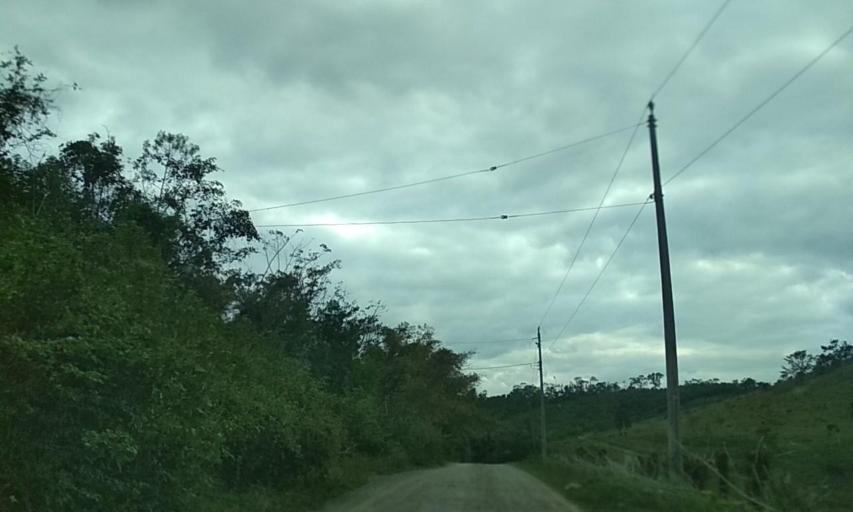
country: MX
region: Veracruz
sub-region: Papantla
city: Polutla
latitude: 20.5077
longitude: -97.2998
